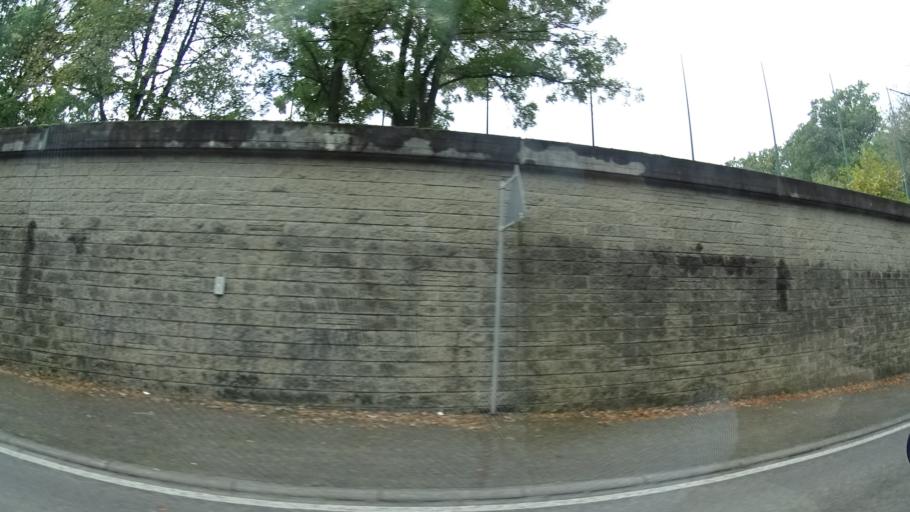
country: DE
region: Baden-Wuerttemberg
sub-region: Karlsruhe Region
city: Ostringen
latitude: 49.2238
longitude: 8.7100
